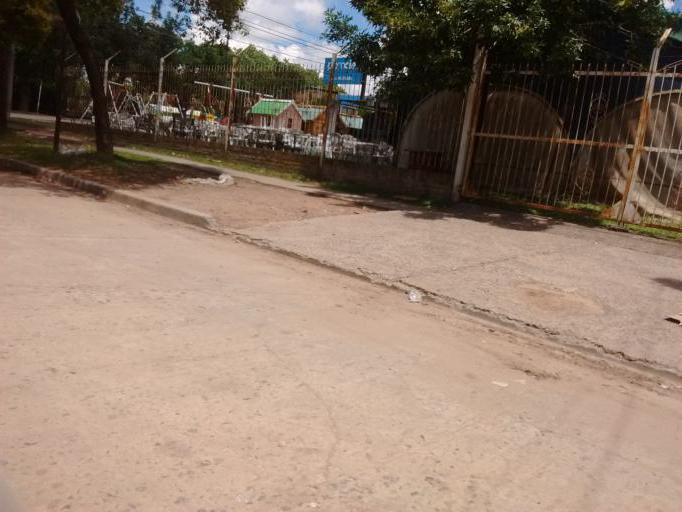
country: AR
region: Santa Fe
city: Funes
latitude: -32.9216
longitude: -60.8085
